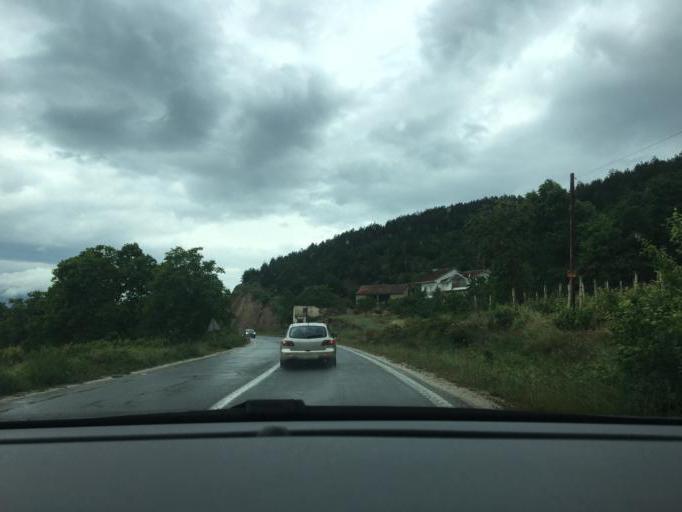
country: MK
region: Debarca
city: Meseista
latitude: 41.2016
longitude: 20.7552
